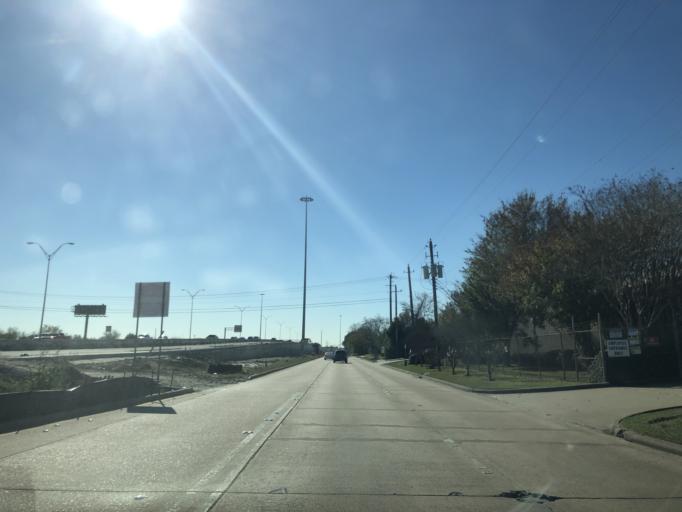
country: US
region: Texas
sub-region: Harris County
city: Deer Park
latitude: 29.6939
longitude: -95.1540
